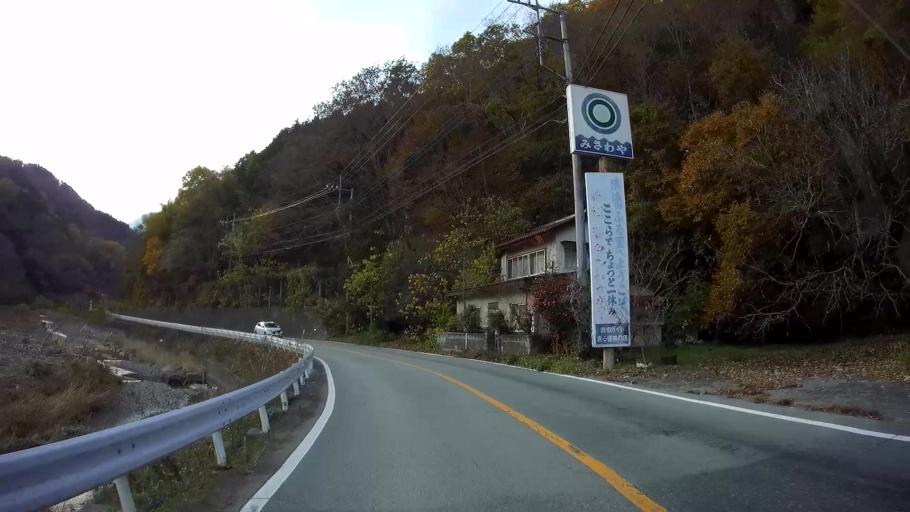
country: JP
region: Yamanashi
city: Ryuo
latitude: 35.4818
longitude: 138.4654
